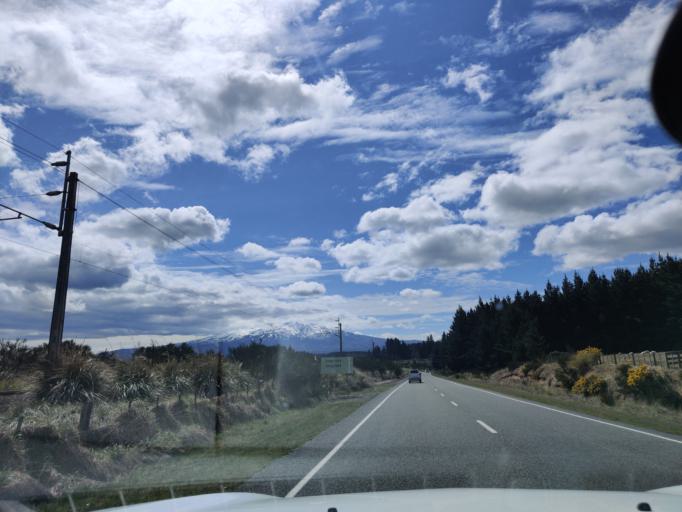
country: NZ
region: Manawatu-Wanganui
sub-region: Ruapehu District
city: Waiouru
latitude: -39.4722
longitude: 175.6646
